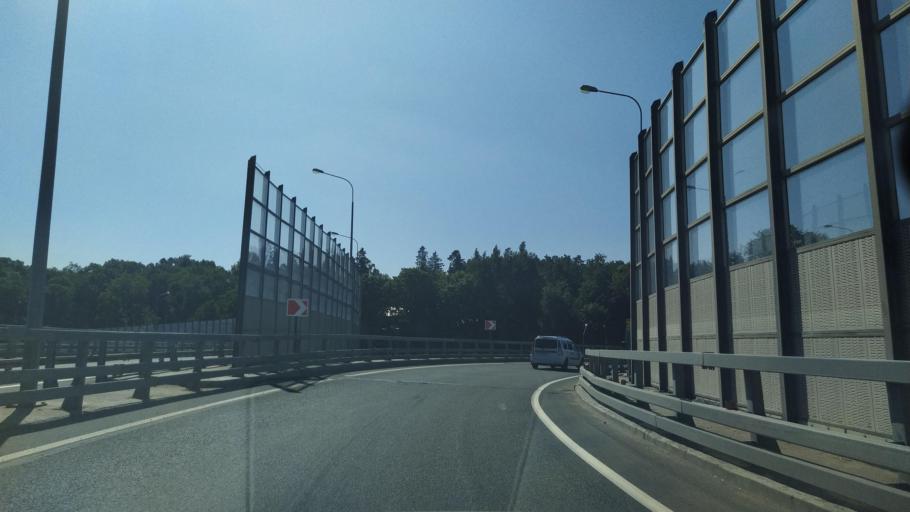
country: RU
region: St.-Petersburg
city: Bol'shaya Izhora
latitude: 59.9275
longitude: 29.6721
